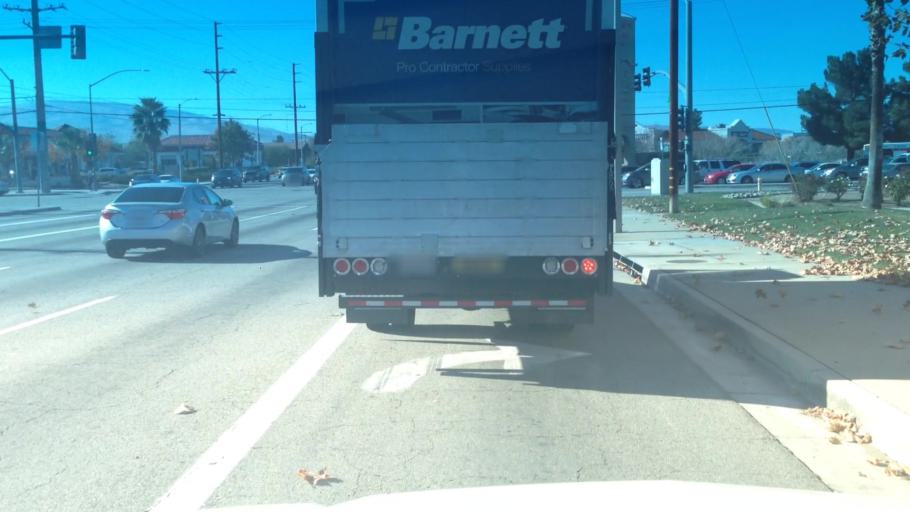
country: US
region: California
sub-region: Los Angeles County
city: Desert View Highlands
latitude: 34.6019
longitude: -118.1470
